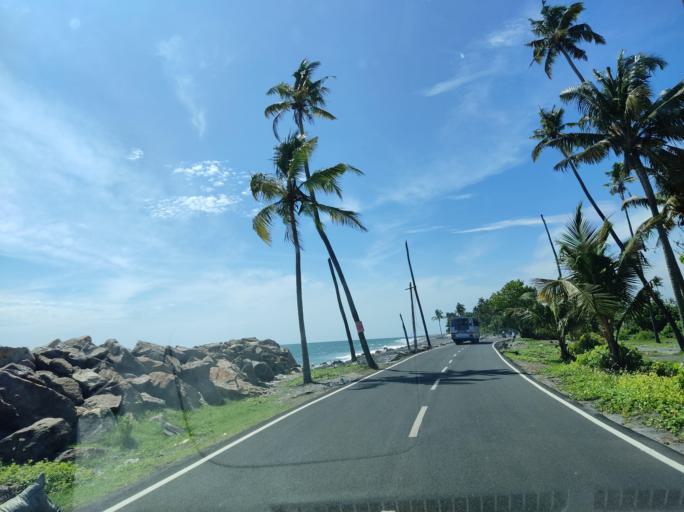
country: IN
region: Kerala
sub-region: Alappuzha
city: Kayankulam
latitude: 9.1665
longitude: 76.4496
